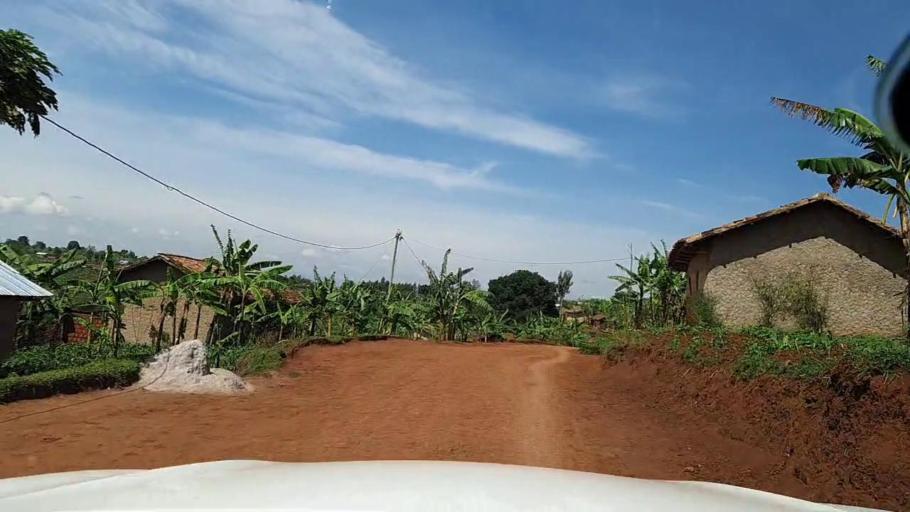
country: RW
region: Southern Province
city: Butare
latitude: -2.7054
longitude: 29.8440
